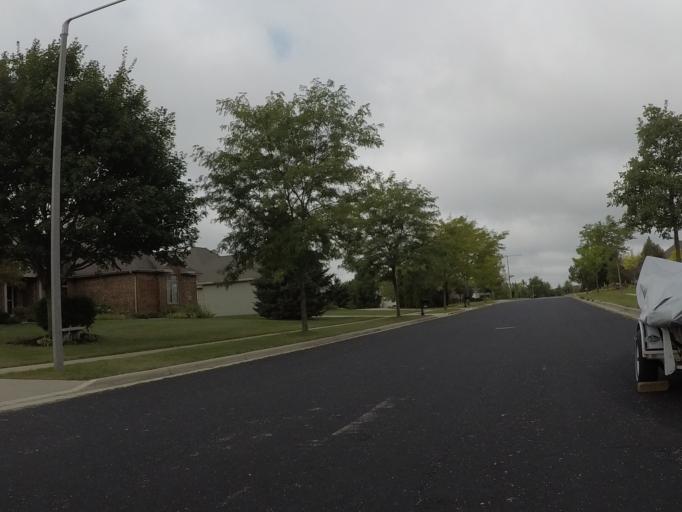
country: US
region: Wisconsin
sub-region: Dane County
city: Verona
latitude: 43.0415
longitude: -89.5465
